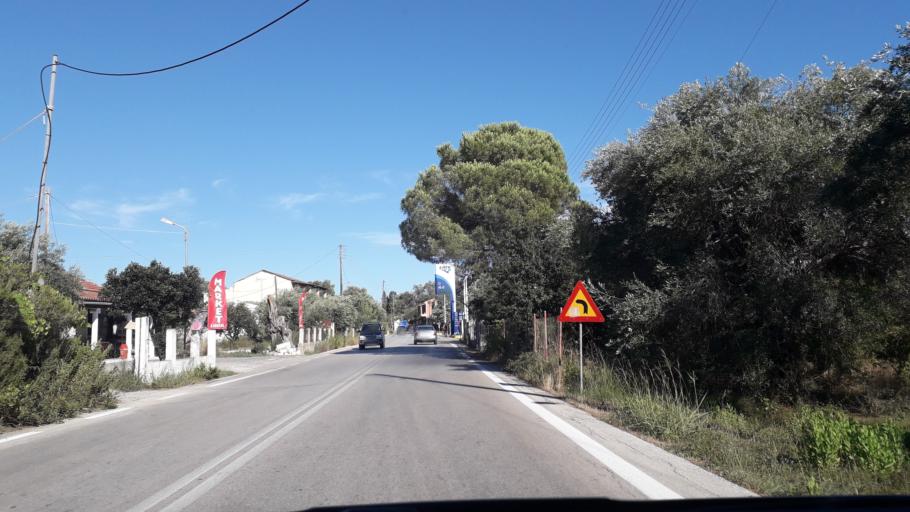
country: GR
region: Ionian Islands
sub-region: Nomos Kerkyras
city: Perivoli
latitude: 39.4438
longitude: 19.9409
